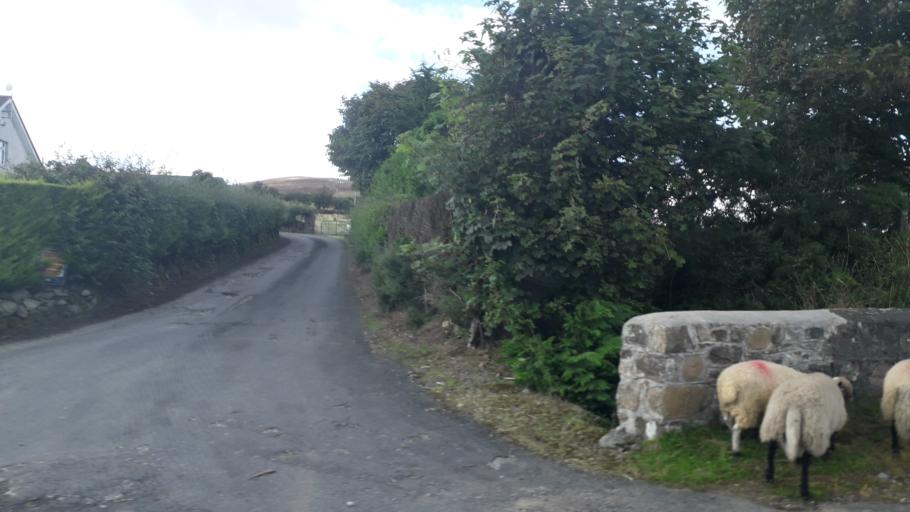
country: GB
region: Northern Ireland
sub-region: Down District
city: Warrenpoint
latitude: 54.0378
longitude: -6.2678
